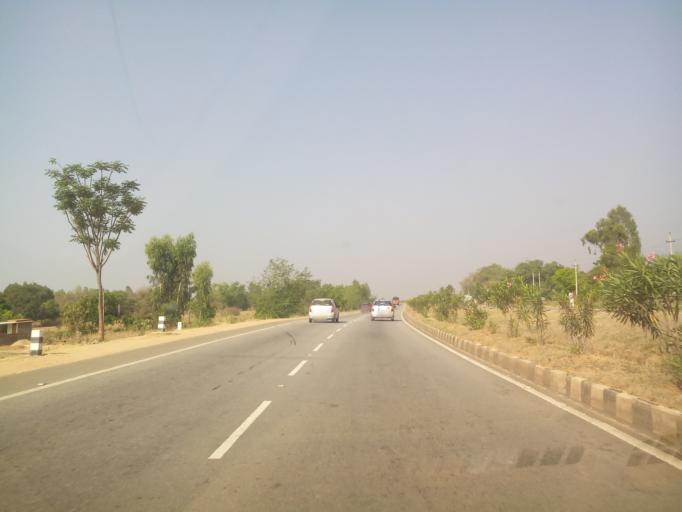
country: IN
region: Karnataka
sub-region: Tumkur
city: Kunigal
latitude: 13.0428
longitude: 77.1318
